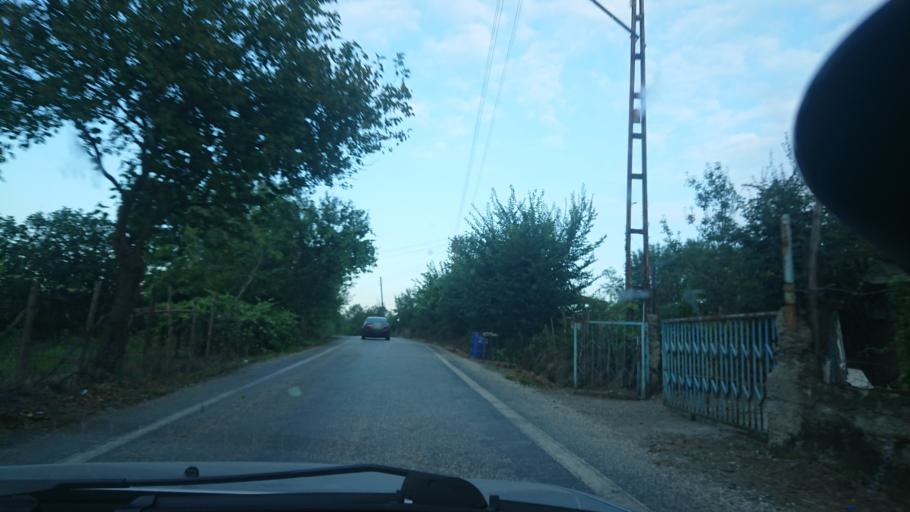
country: TR
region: Samsun
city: Tekkekoy
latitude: 41.1717
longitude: 36.5328
